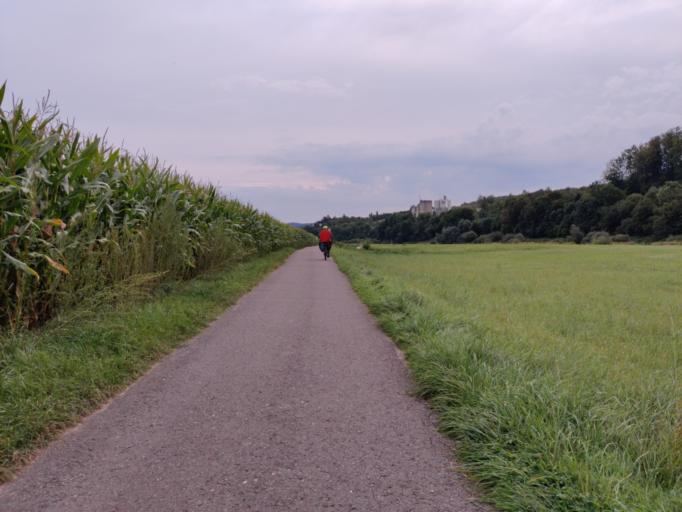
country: DE
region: Lower Saxony
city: Hehlen
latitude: 51.9867
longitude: 9.4494
